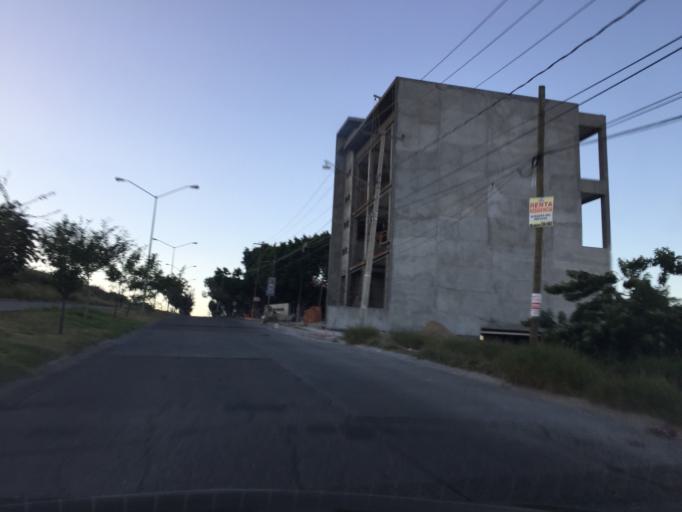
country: MX
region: Guanajuato
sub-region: Leon
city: La Ermita
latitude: 21.1617
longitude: -101.7083
